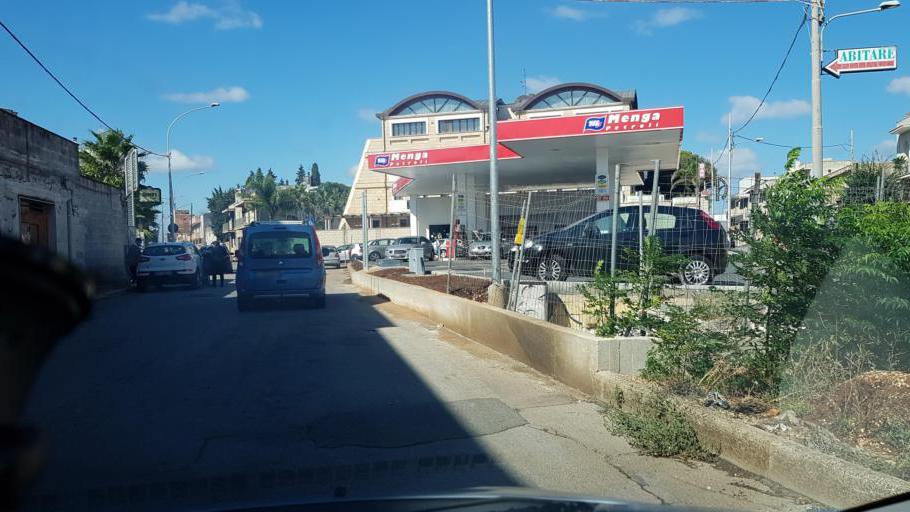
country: IT
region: Apulia
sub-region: Provincia di Brindisi
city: San Vito dei Normanni
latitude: 40.6521
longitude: 17.7120
